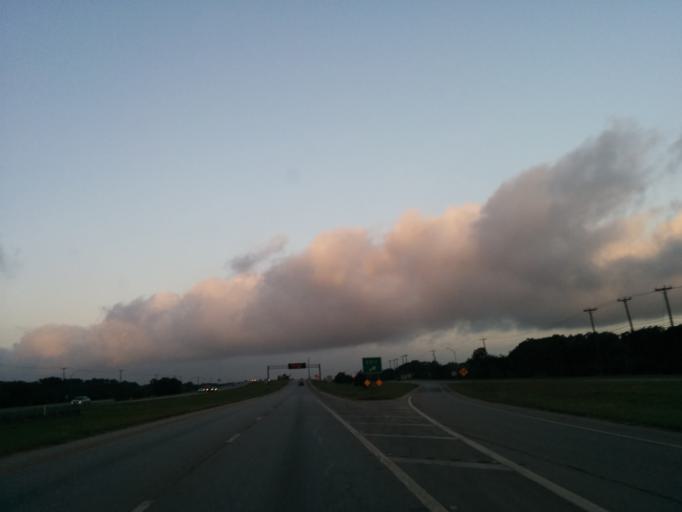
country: US
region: Texas
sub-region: Bexar County
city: Helotes
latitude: 29.5816
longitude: -98.6413
